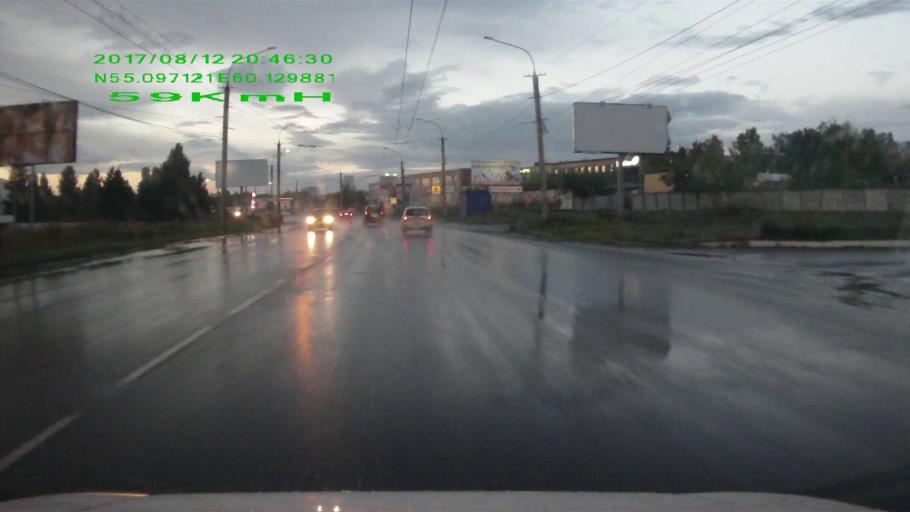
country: RU
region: Chelyabinsk
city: Turgoyak
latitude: 55.0972
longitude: 60.1300
